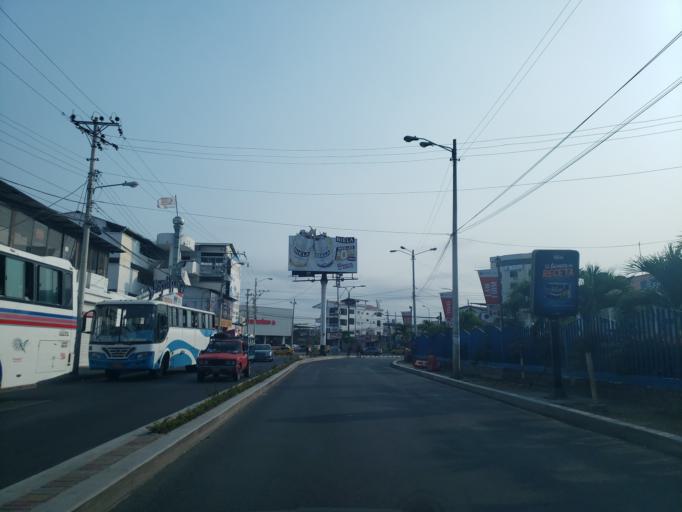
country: EC
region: Manabi
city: Manta
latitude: -0.9440
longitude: -80.7337
